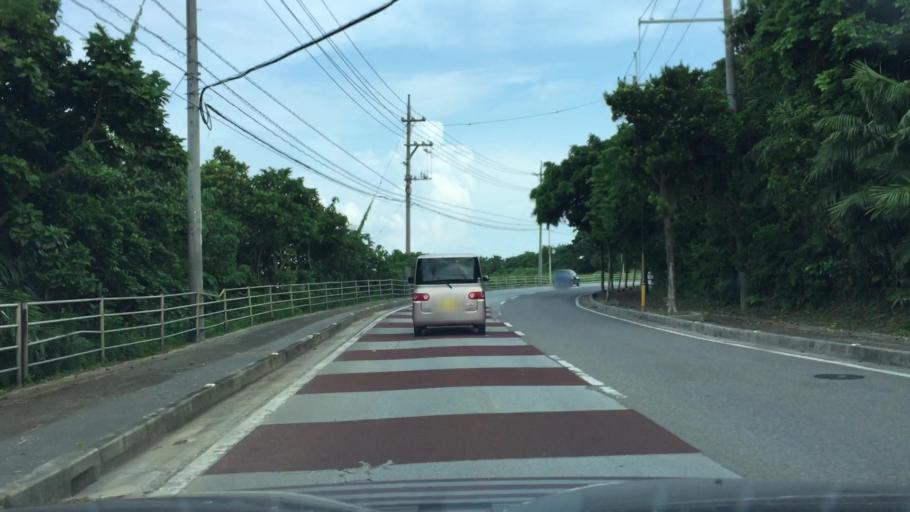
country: JP
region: Okinawa
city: Ishigaki
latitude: 24.4416
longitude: 124.2490
